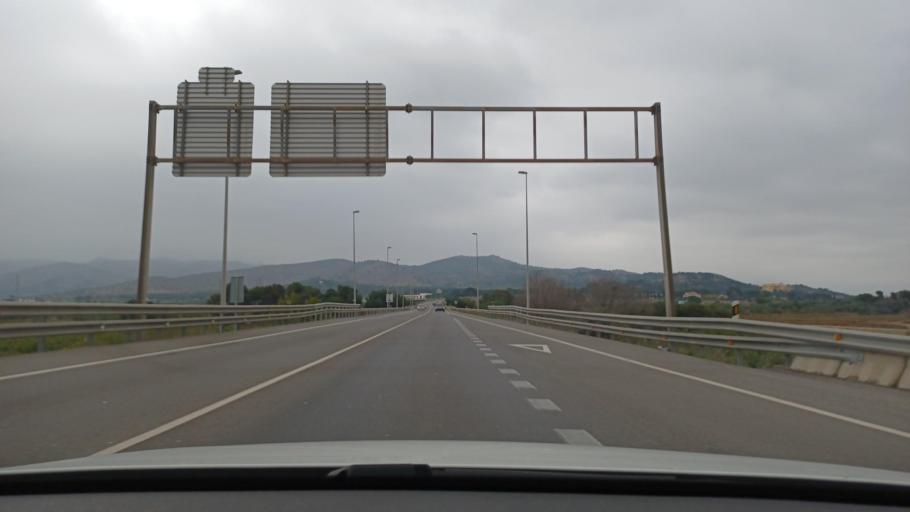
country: ES
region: Valencia
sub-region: Provincia de Castello
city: Borriol
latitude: 39.9961
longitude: -0.0887
